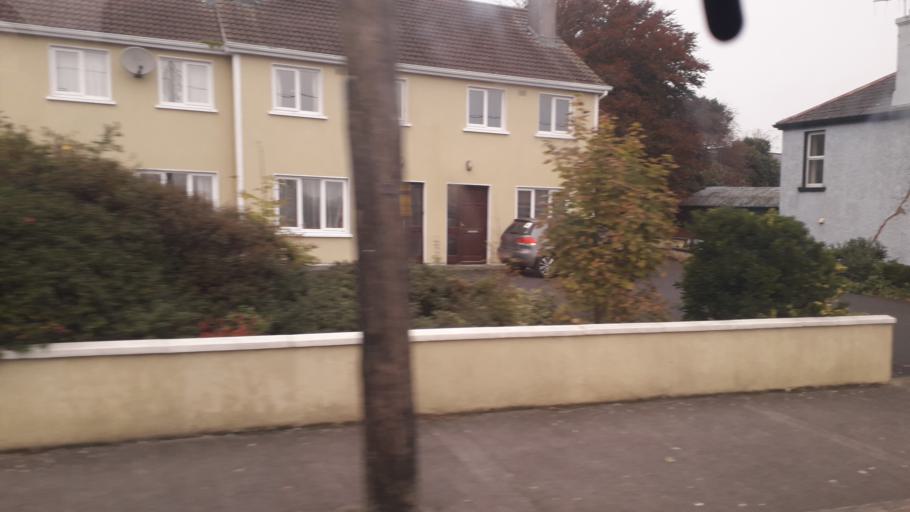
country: IE
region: Leinster
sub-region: Uibh Fhaili
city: Birr
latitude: 52.9840
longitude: -7.9253
